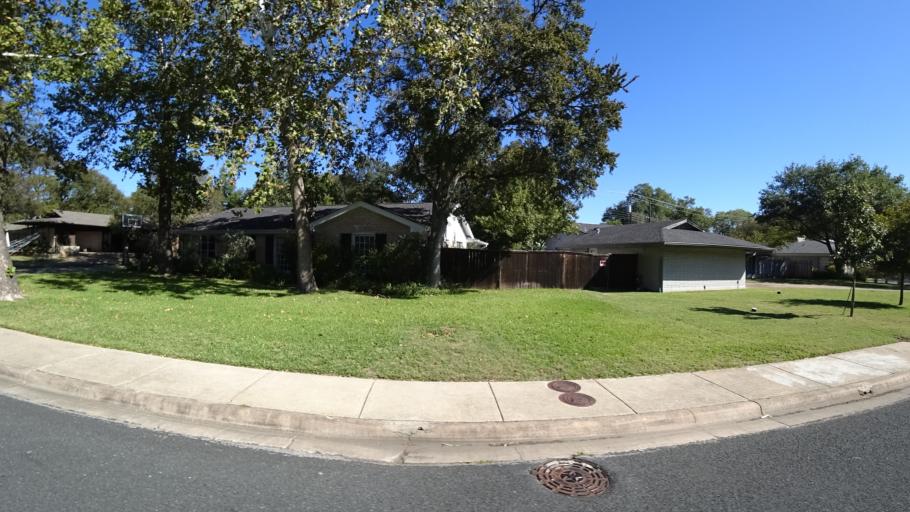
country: US
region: Texas
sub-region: Travis County
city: West Lake Hills
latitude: 30.3576
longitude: -97.7678
